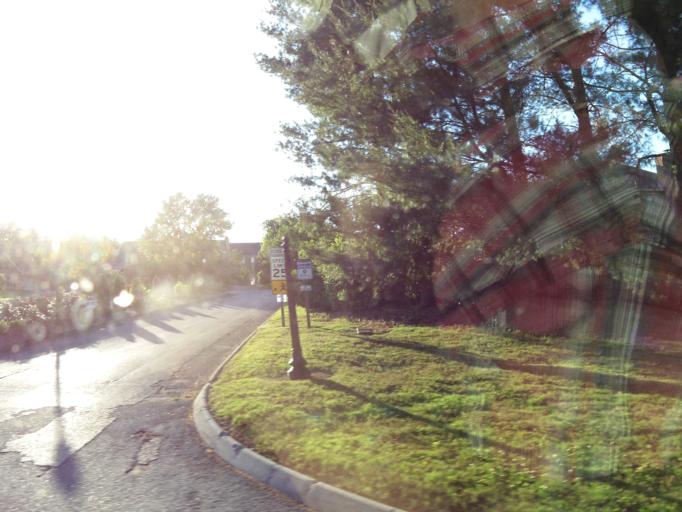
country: US
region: Tennessee
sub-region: Knox County
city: Farragut
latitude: 35.8646
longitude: -84.1166
